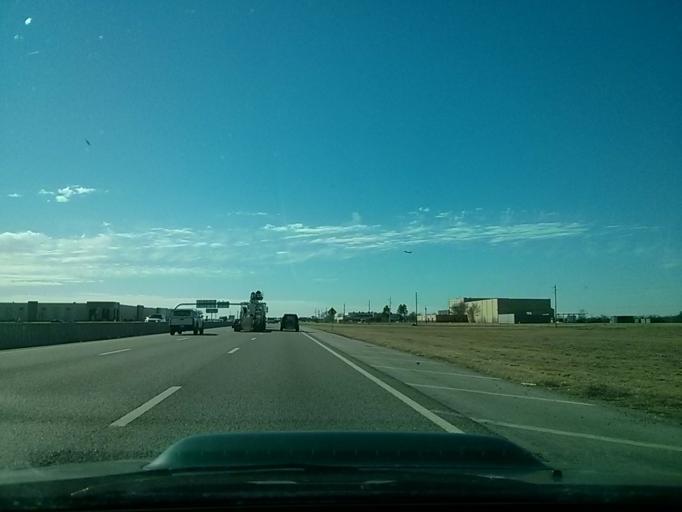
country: US
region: Oklahoma
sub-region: Tulsa County
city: Owasso
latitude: 36.2197
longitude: -95.8518
